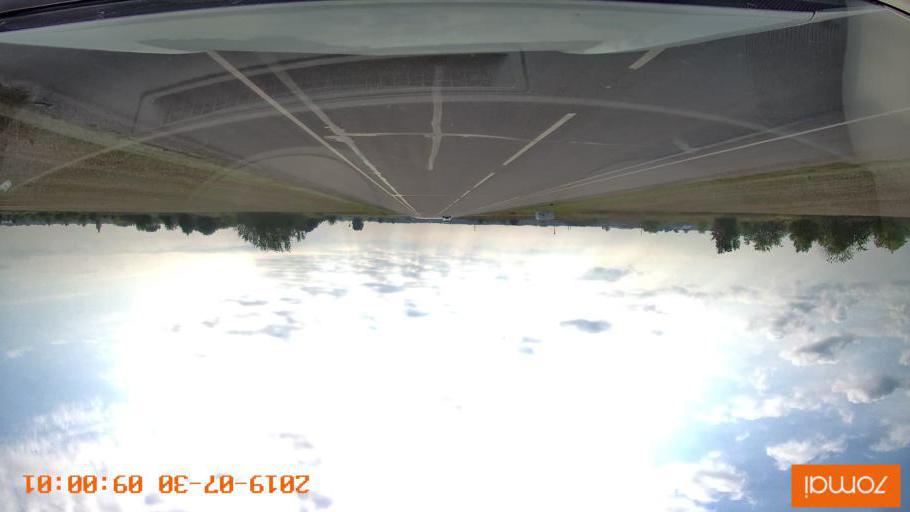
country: RU
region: Kaliningrad
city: Gusev
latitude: 54.6150
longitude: 22.1699
